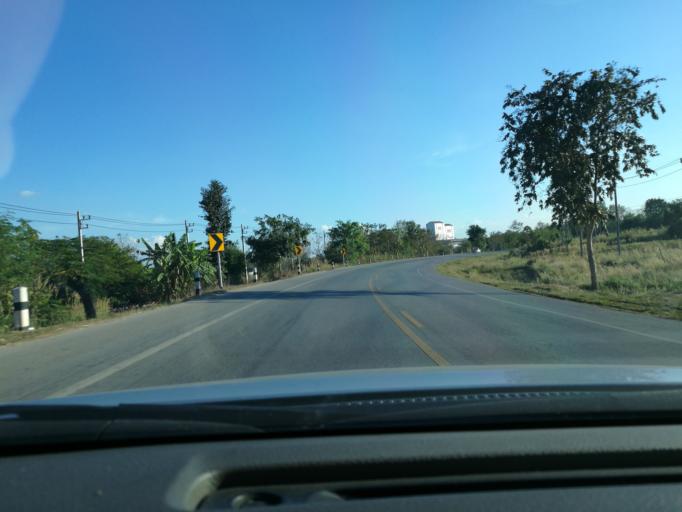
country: TH
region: Phitsanulok
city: Nakhon Thai
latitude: 17.0545
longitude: 100.8112
